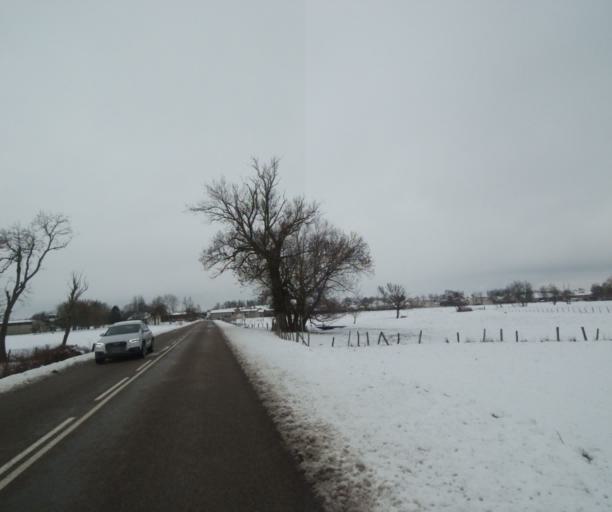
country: FR
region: Champagne-Ardenne
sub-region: Departement de la Haute-Marne
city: Montier-en-Der
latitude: 48.4761
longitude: 4.7862
